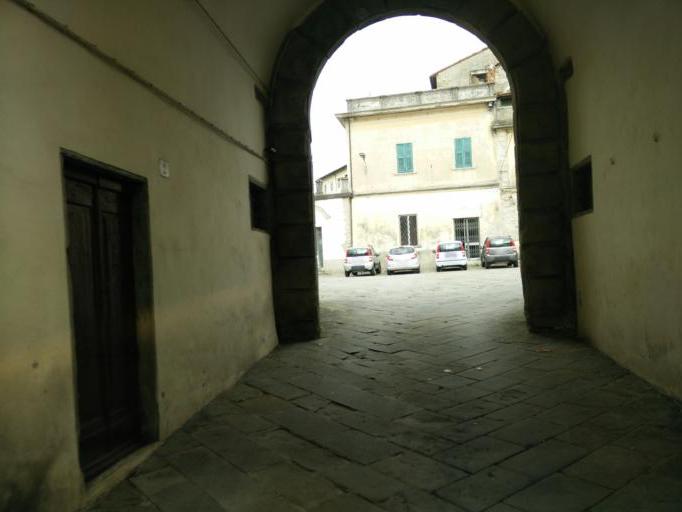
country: IT
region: Tuscany
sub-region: Provincia di Massa-Carrara
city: Fivizzano
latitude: 44.2364
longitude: 10.1219
